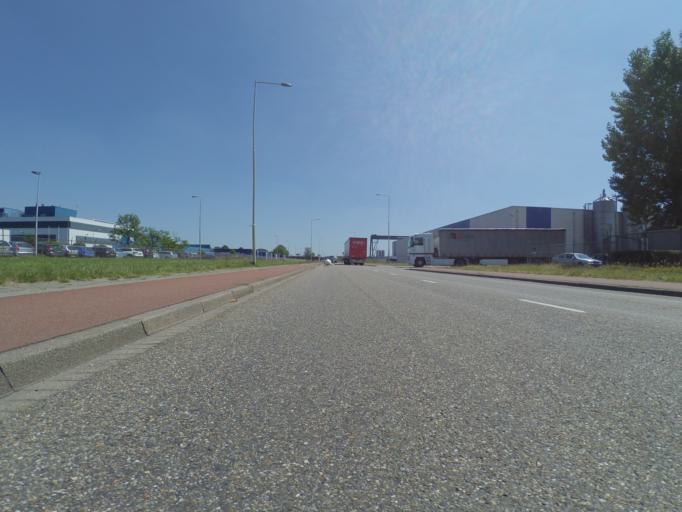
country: NL
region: North Brabant
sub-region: Gemeente Bergen op Zoom
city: Halsteren
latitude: 51.5086
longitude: 4.2634
